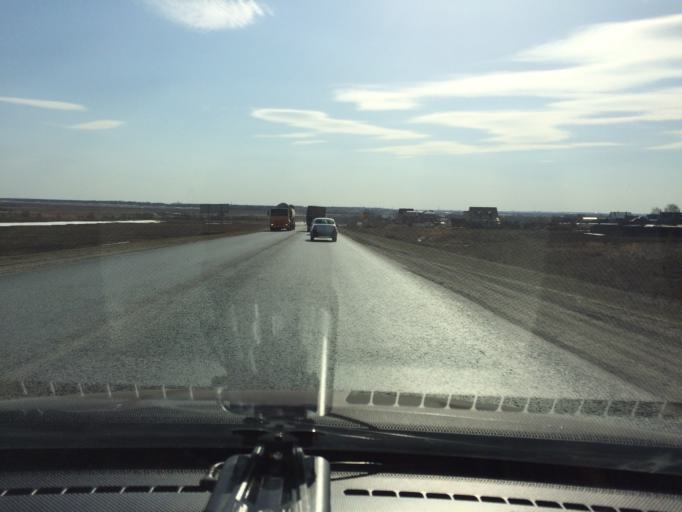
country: RU
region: Mariy-El
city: Yoshkar-Ola
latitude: 56.6940
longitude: 48.0562
